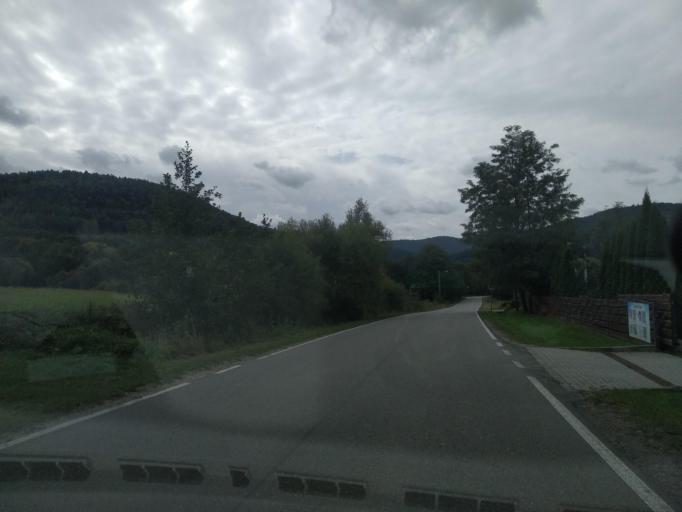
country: PL
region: Lesser Poland Voivodeship
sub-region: Powiat gorlicki
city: Ropa
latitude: 49.5791
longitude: 21.1006
